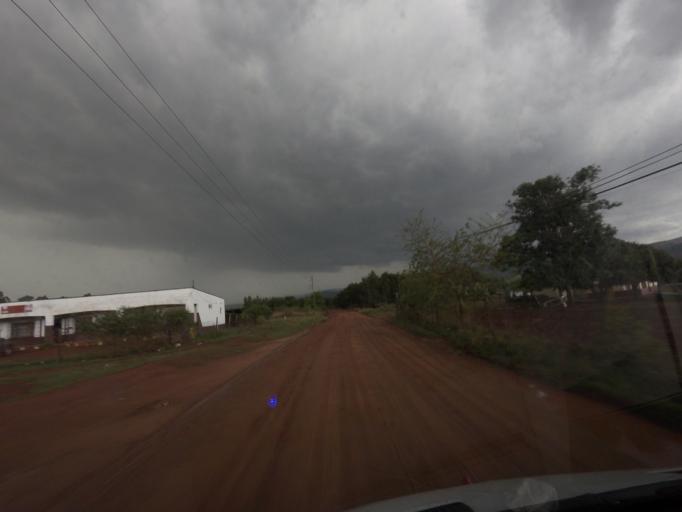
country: SZ
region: Hhohho
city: Lobamba
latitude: -26.4717
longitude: 31.2054
